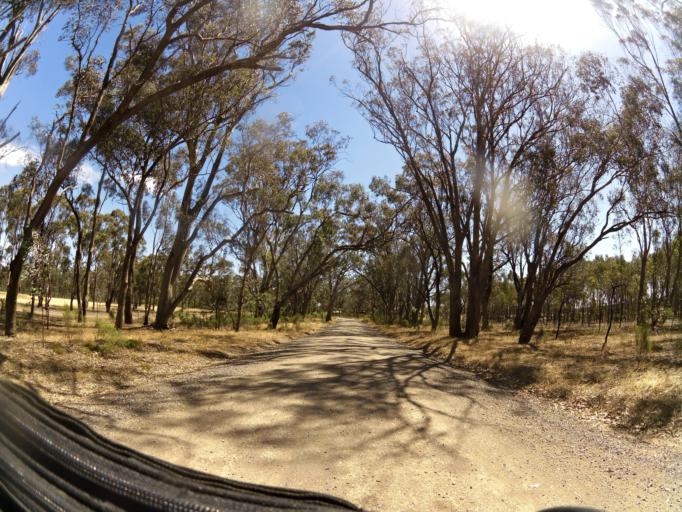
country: AU
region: Victoria
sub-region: Campaspe
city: Kyabram
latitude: -36.8418
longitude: 145.0686
